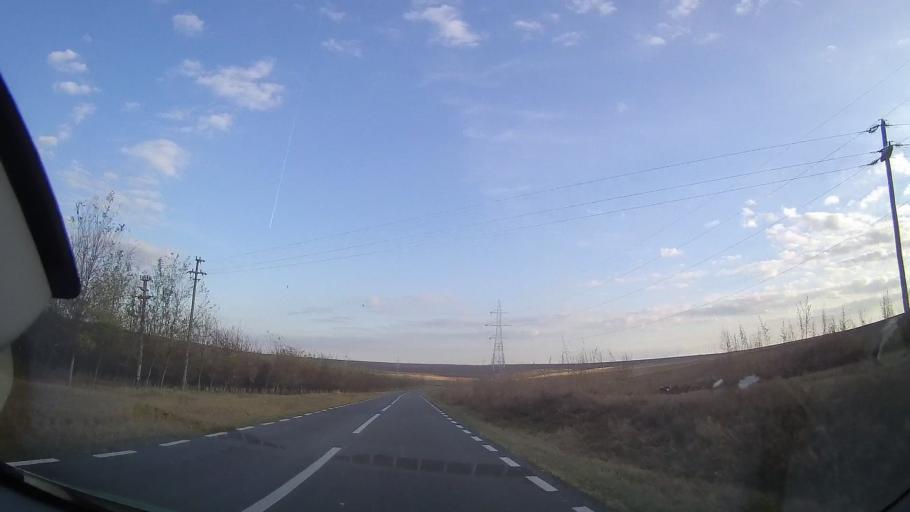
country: RO
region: Constanta
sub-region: Comuna Chirnogeni
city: Plopeni
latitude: 43.9576
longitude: 28.1475
